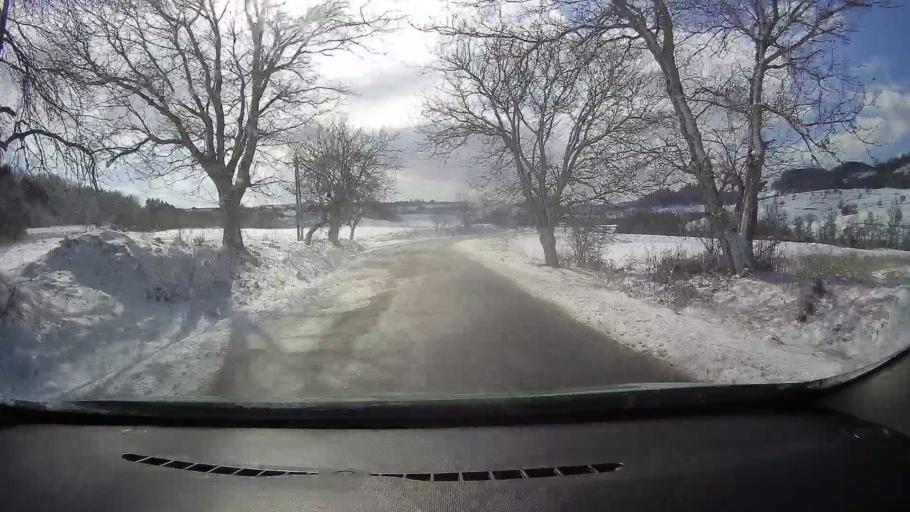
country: RO
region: Sibiu
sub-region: Comuna Mihaileni
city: Mihaileni
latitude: 46.0200
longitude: 24.3891
